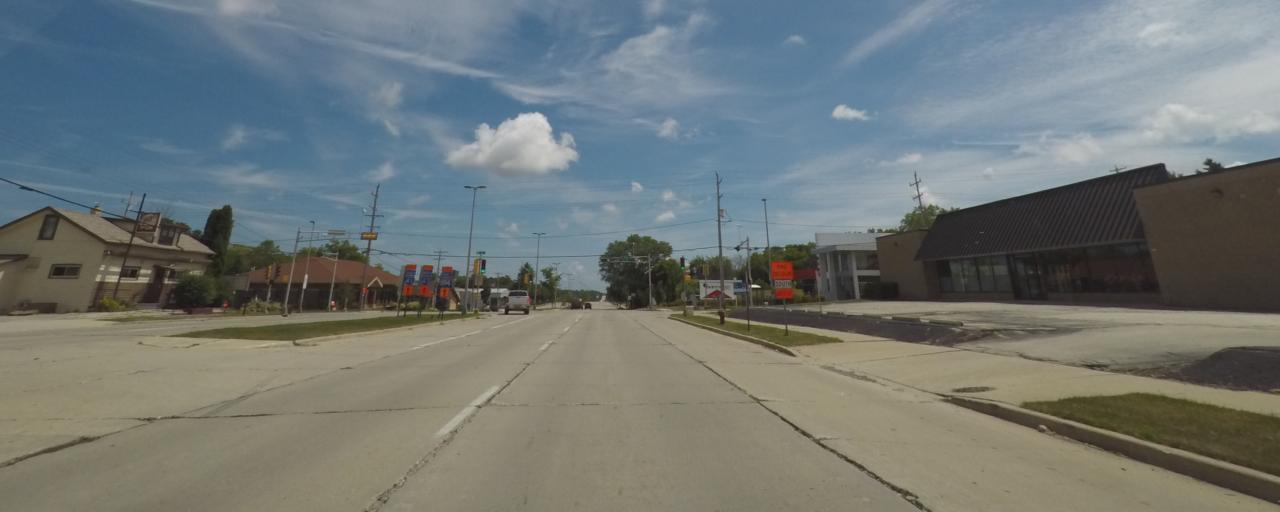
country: US
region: Wisconsin
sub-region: Milwaukee County
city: Greenfield
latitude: 42.9592
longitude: -87.9993
